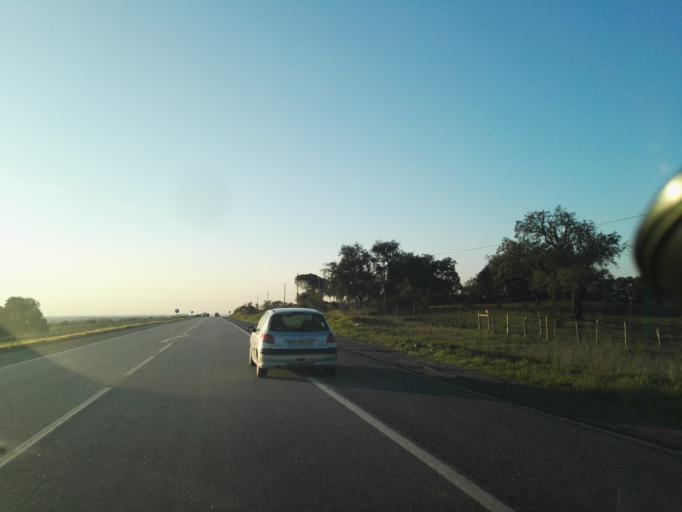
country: PT
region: Evora
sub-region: Montemor-O-Novo
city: Montemor-o-Novo
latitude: 38.6462
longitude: -8.3136
